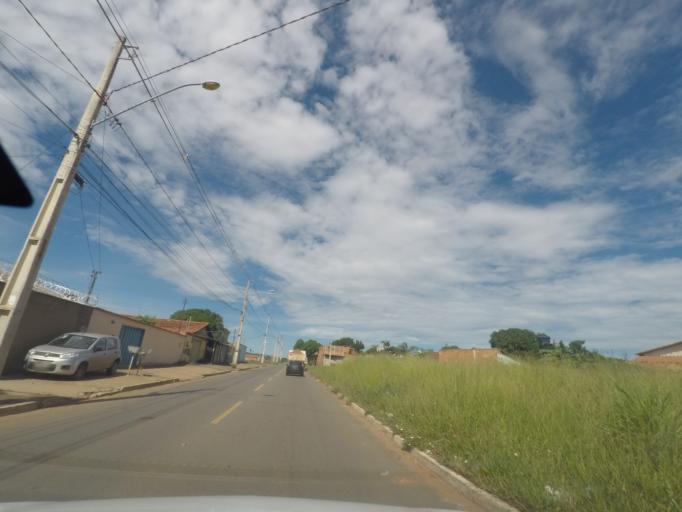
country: BR
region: Goias
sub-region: Aparecida De Goiania
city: Aparecida de Goiania
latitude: -16.8128
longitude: -49.2851
